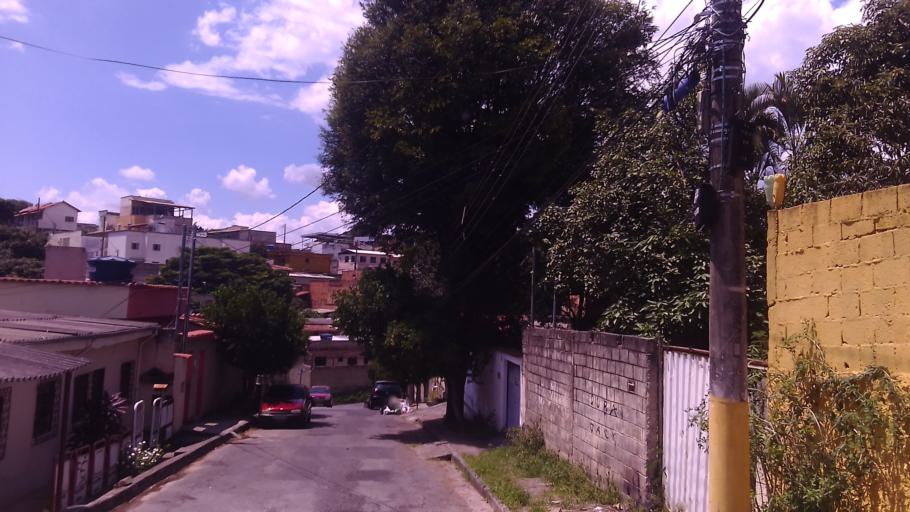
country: BR
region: Minas Gerais
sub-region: Belo Horizonte
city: Belo Horizonte
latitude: -19.8615
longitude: -43.9038
